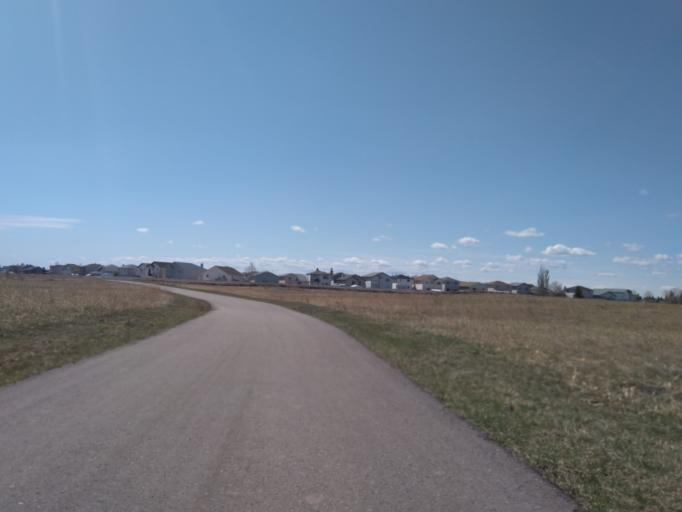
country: CA
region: Alberta
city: Chestermere
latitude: 51.0533
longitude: -113.9234
